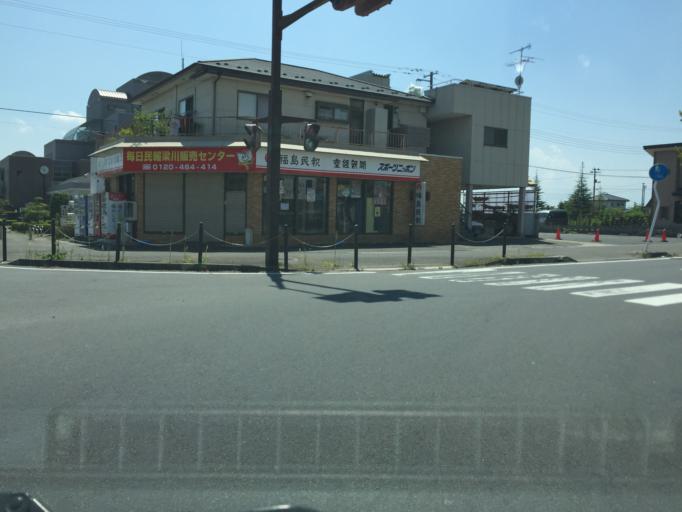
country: JP
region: Fukushima
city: Yanagawamachi-saiwaicho
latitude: 37.8466
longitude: 140.6021
